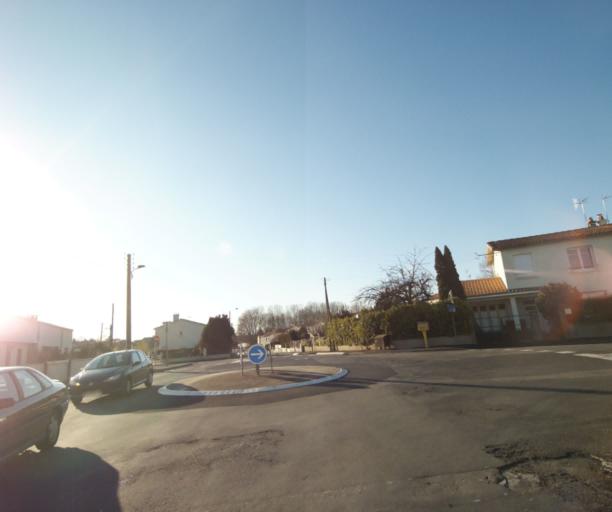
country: FR
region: Poitou-Charentes
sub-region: Departement des Deux-Sevres
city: Niort
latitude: 46.3330
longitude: -0.4743
